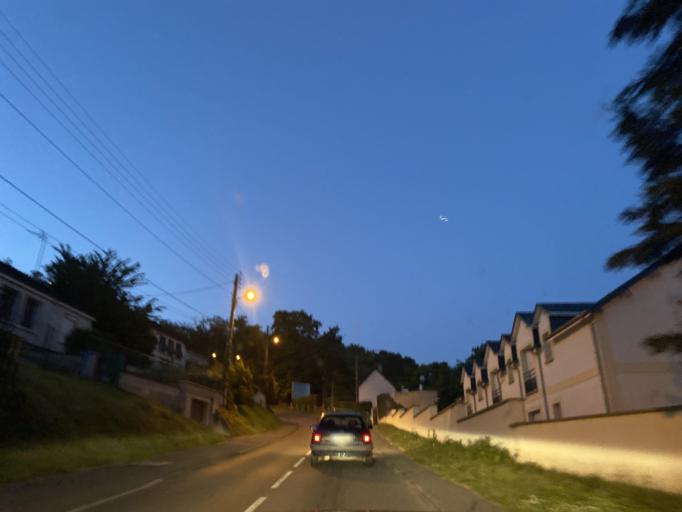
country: FR
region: Haute-Normandie
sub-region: Departement de l'Eure
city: Evreux
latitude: 49.0280
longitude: 1.1672
